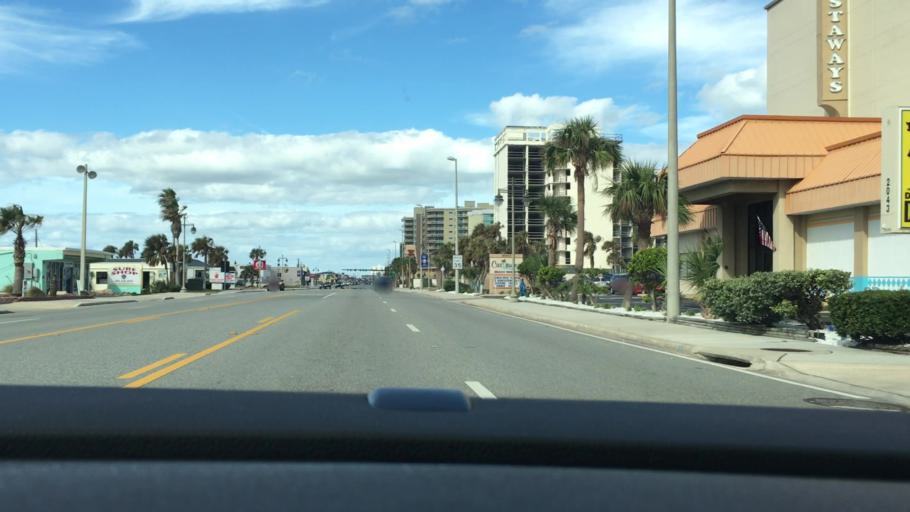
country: US
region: Florida
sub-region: Volusia County
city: Daytona Beach Shores
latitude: 29.1997
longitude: -80.9948
